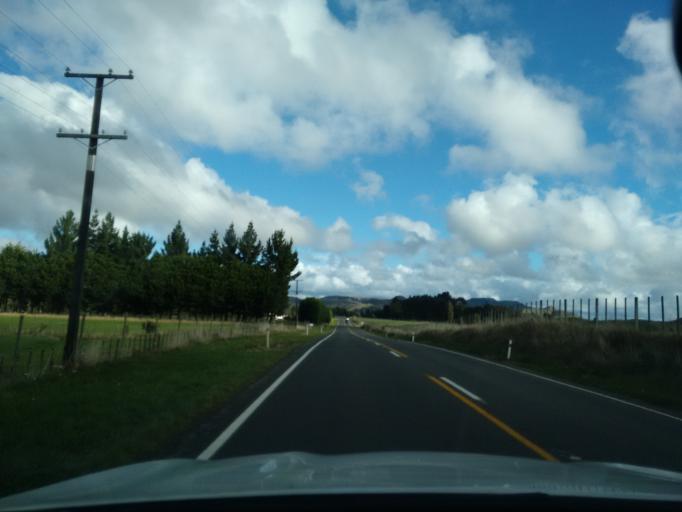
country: NZ
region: Manawatu-Wanganui
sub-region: Ruapehu District
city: Waiouru
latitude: -39.4108
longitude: 175.2844
